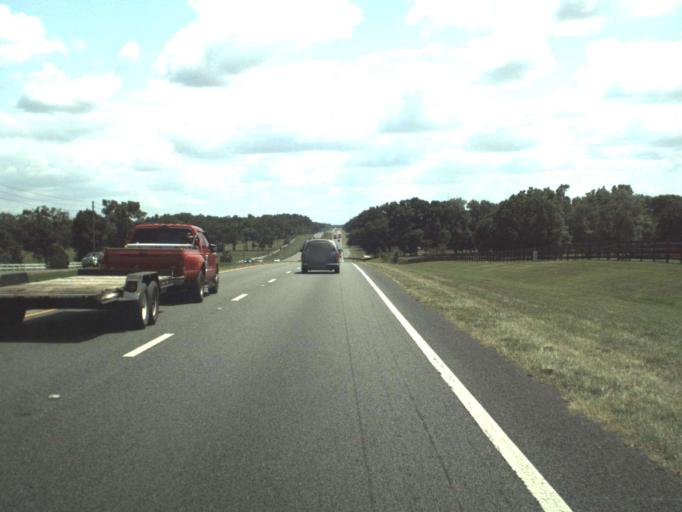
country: US
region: Florida
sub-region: Marion County
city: Ocala
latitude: 29.2876
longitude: -82.1520
